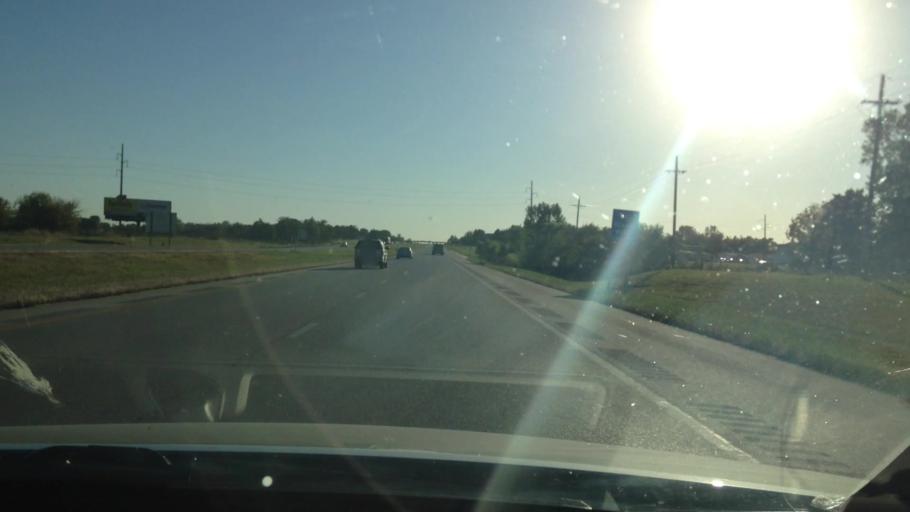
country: US
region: Kansas
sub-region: Johnson County
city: Gardner
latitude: 38.8061
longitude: -94.8935
